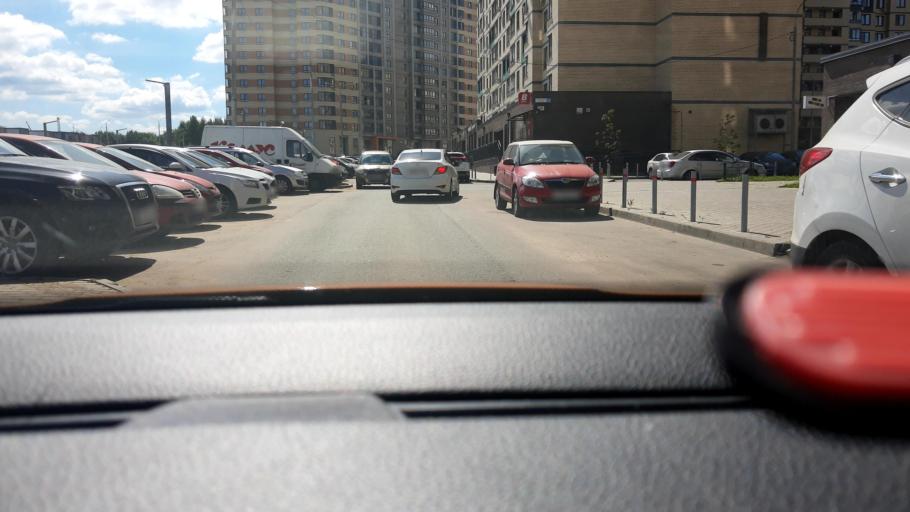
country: RU
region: Moskovskaya
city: Mytishchi
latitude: 55.9264
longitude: 37.7301
